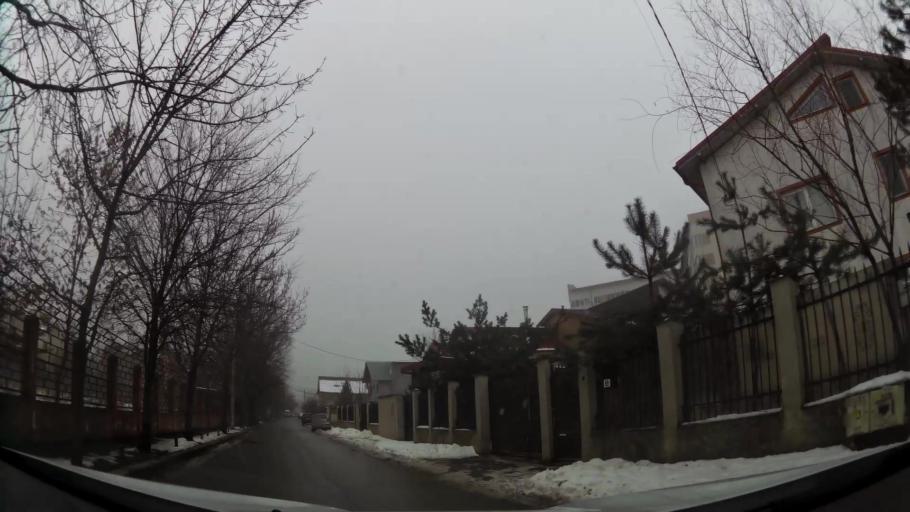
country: RO
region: Ilfov
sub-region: Comuna Chiajna
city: Rosu
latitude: 44.4374
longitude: 25.9937
